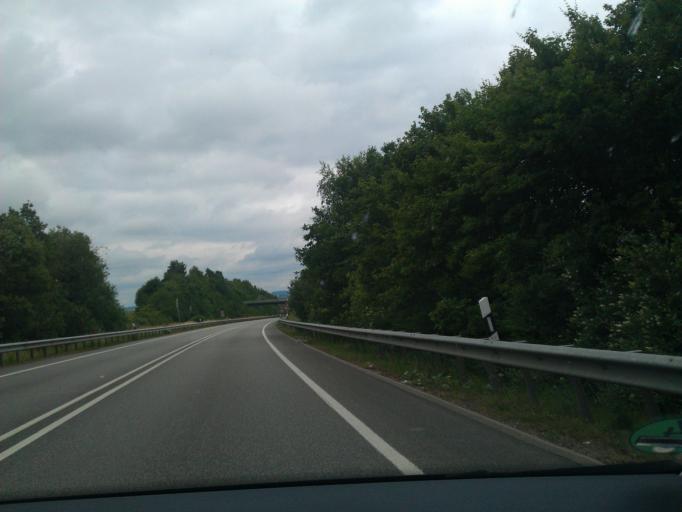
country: DE
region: Rheinland-Pfalz
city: Hohfroschen
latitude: 49.2450
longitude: 7.5694
